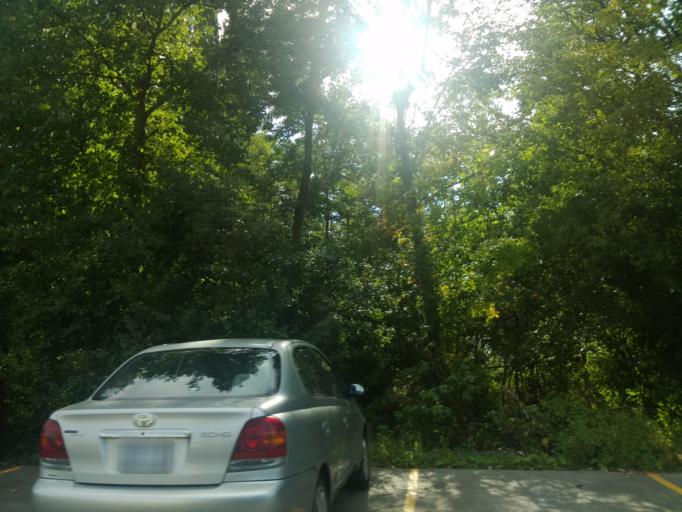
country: CA
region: Ontario
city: Ottawa
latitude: 45.3926
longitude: -75.6468
